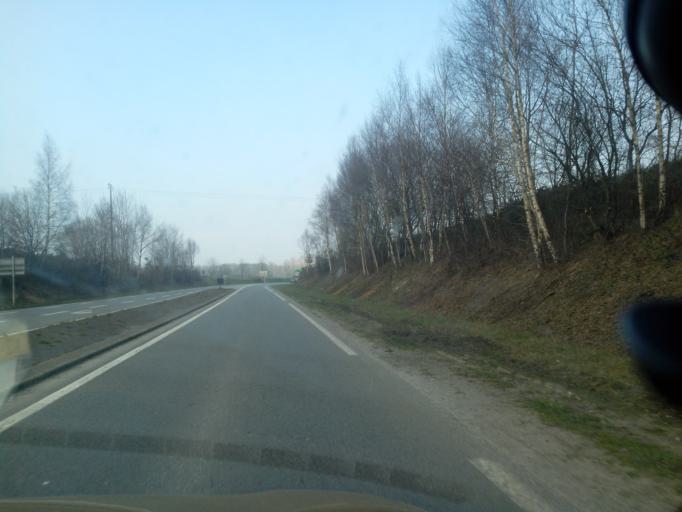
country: FR
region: Brittany
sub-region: Departement d'Ille-et-Vilaine
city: Saint-Meen-le-Grand
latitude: 48.2010
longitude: -2.1745
